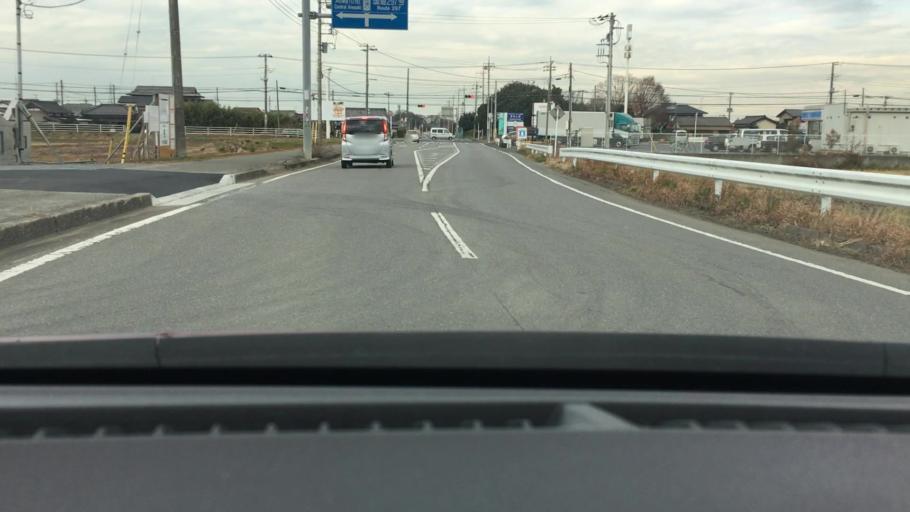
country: JP
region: Chiba
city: Ichihara
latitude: 35.4768
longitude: 140.0610
